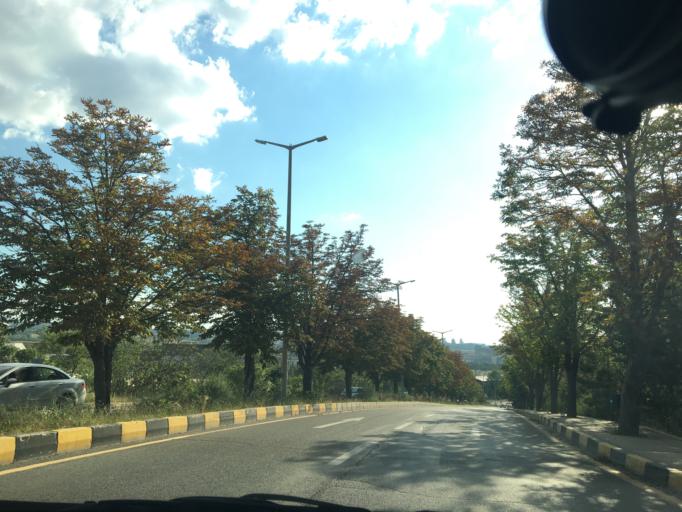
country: TR
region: Ankara
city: Ankara
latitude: 39.8997
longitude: 32.7806
